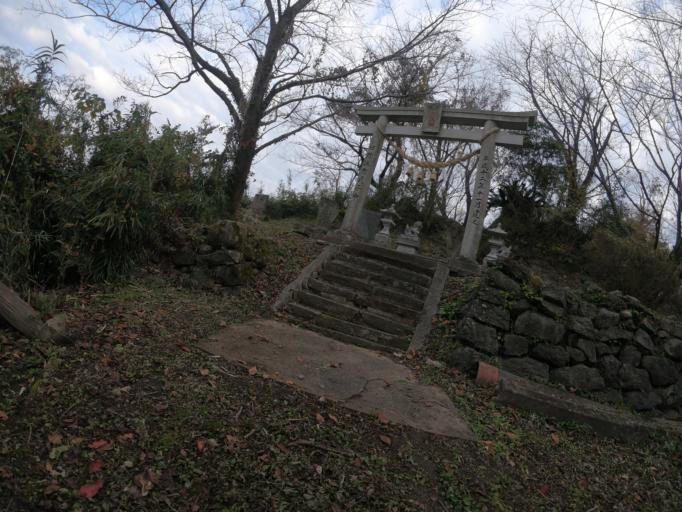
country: JP
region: Nagasaki
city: Shimabara
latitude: 32.6595
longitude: 130.2526
